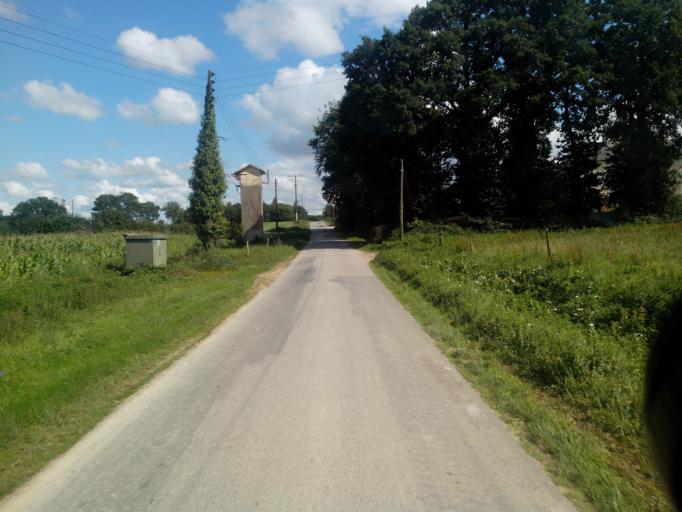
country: FR
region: Brittany
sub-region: Departement du Morbihan
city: Mauron
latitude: 48.1421
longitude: -2.2962
